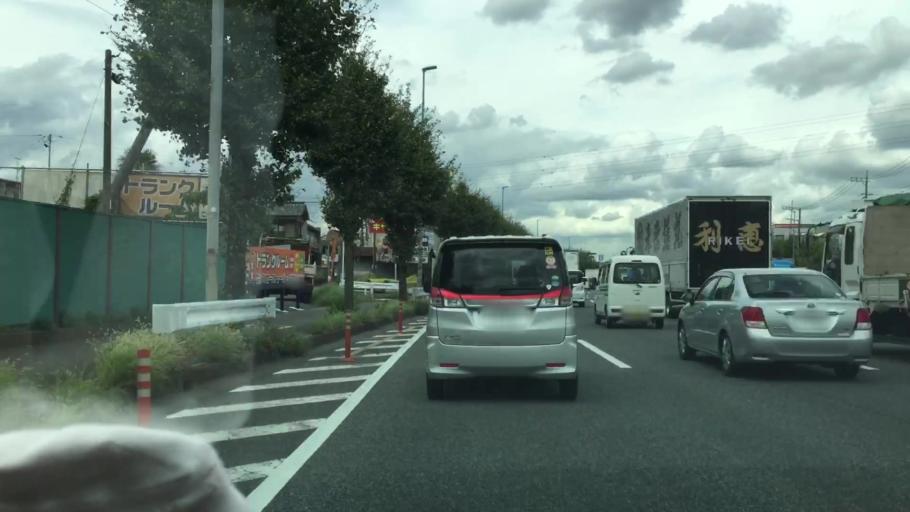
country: JP
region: Saitama
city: Yono
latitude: 35.9110
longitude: 139.5937
